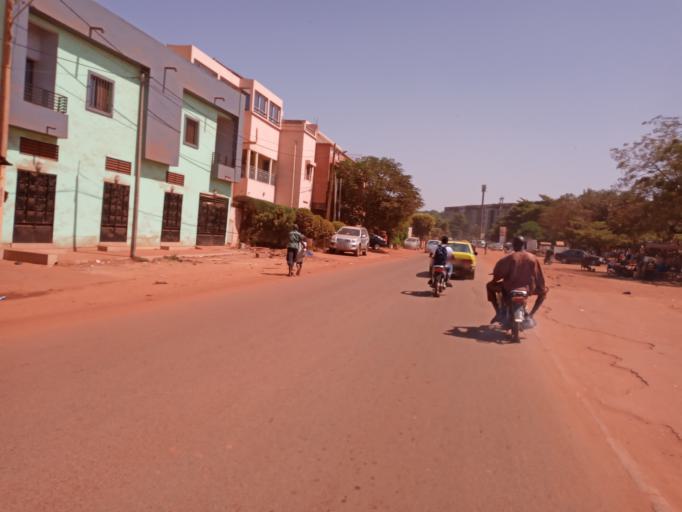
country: ML
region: Bamako
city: Bamako
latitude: 12.6140
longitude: -7.9953
